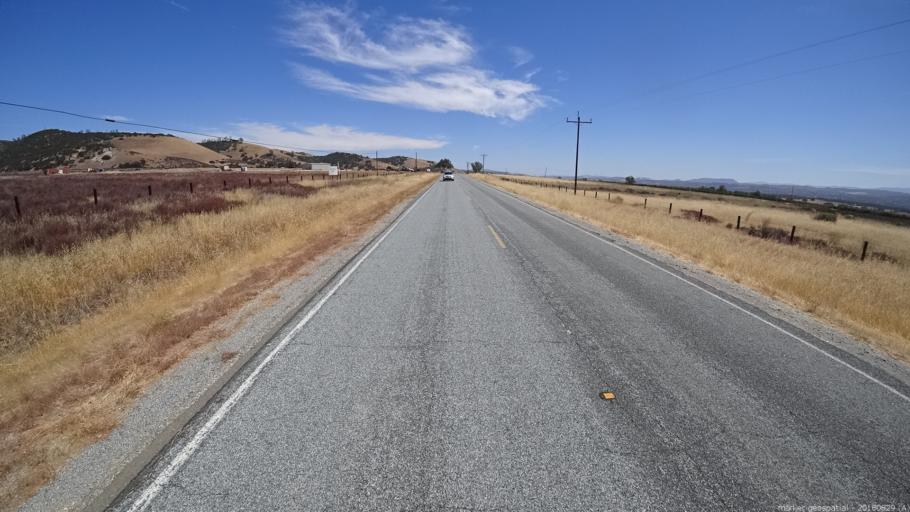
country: US
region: California
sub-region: San Luis Obispo County
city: Lake Nacimiento
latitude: 35.9241
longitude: -121.0405
